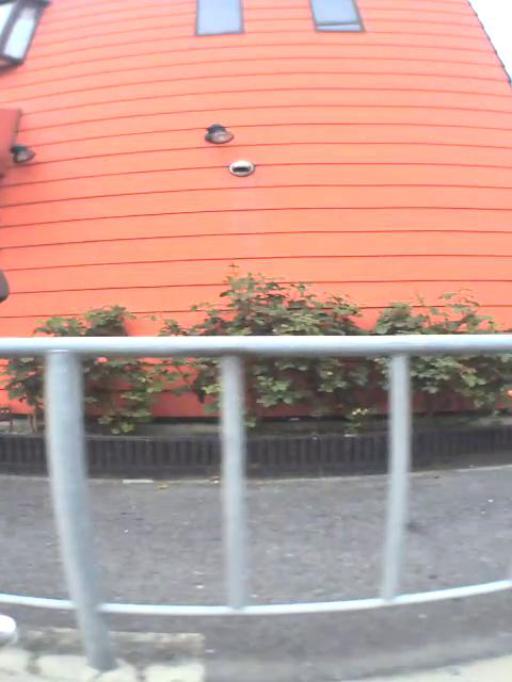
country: JP
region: Osaka
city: Neyagawa
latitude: 34.7497
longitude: 135.6240
